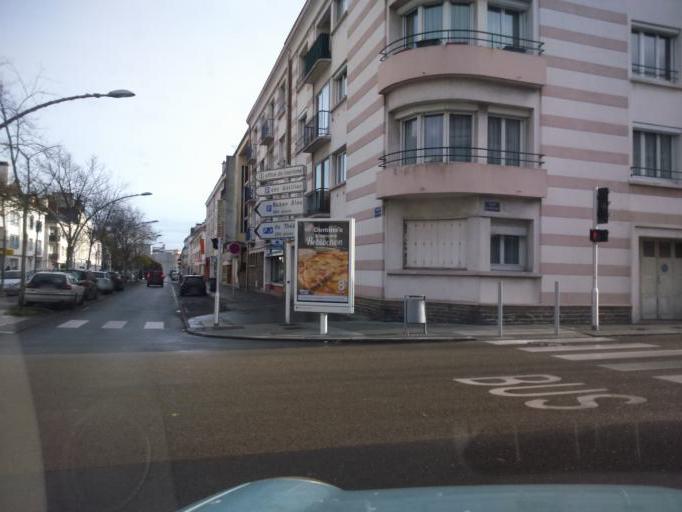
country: FR
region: Pays de la Loire
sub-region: Departement de la Loire-Atlantique
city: Saint-Nazaire
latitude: 47.2783
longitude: -2.2098
